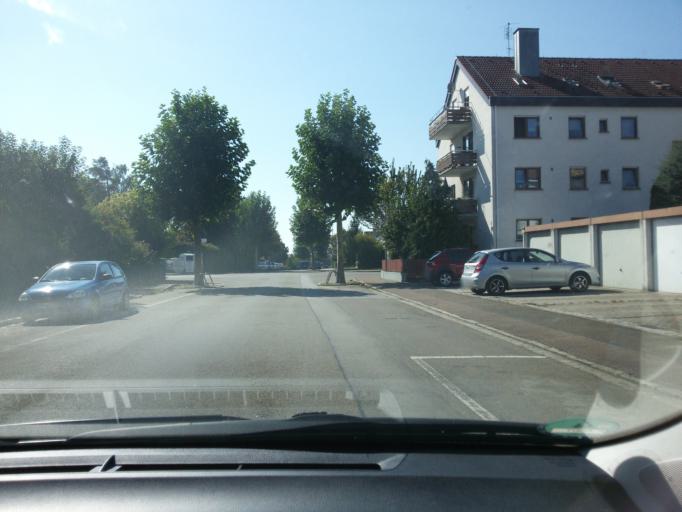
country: DE
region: Bavaria
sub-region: Swabia
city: Oettingen in Bayern
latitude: 48.9549
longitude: 10.5989
